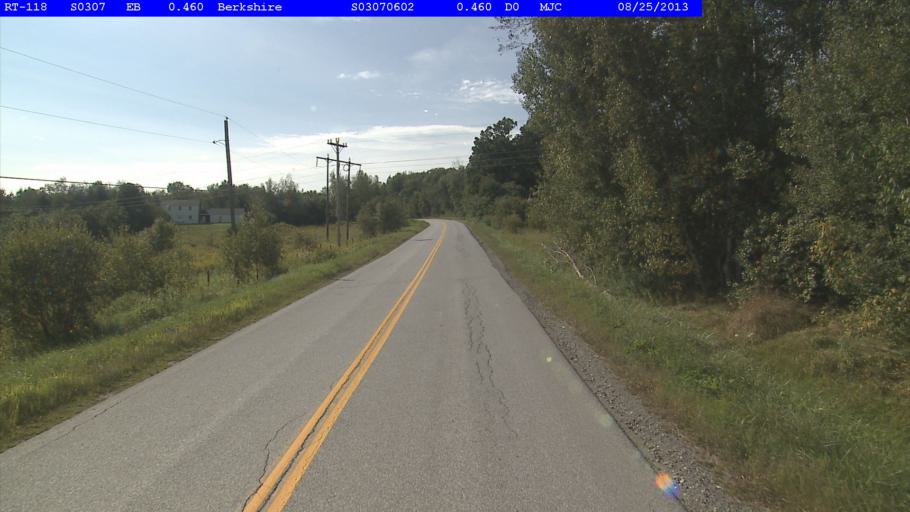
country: US
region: Vermont
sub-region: Franklin County
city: Richford
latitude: 44.9351
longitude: -72.7205
